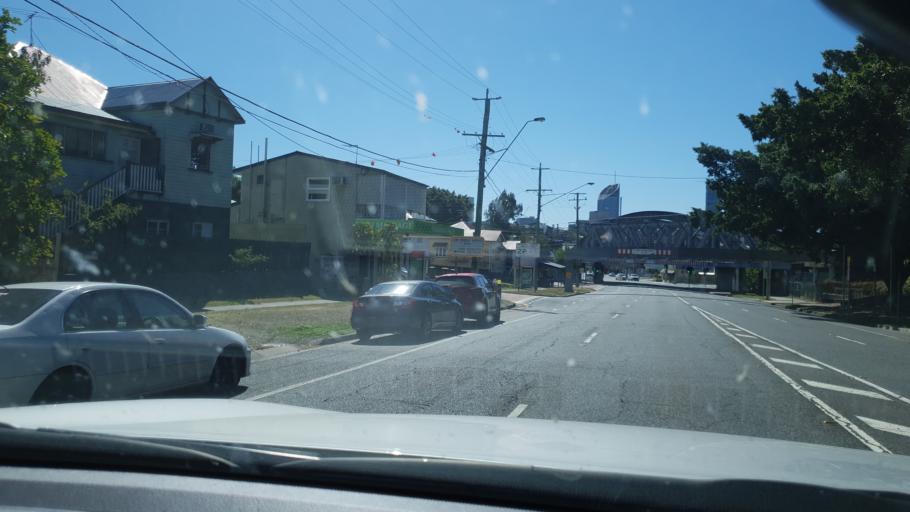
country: AU
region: Queensland
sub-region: Brisbane
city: Woolloongabba
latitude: -27.4932
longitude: 153.0275
